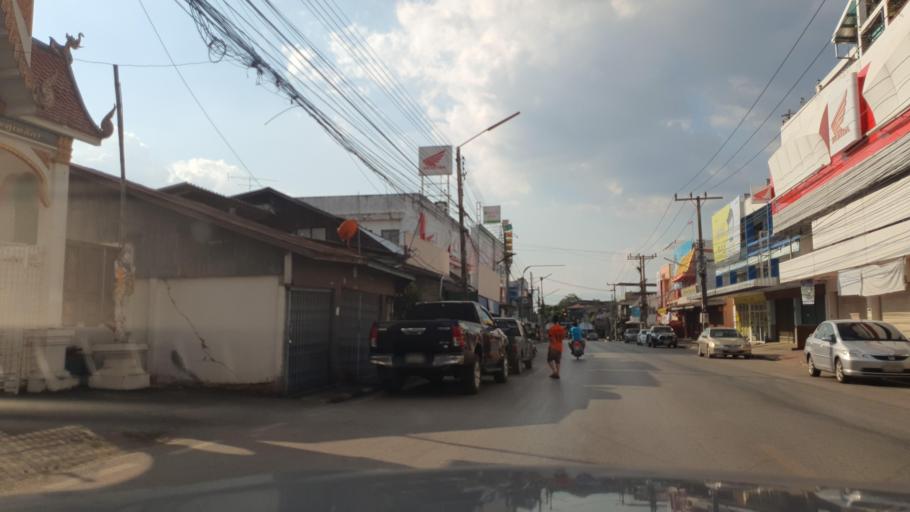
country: TH
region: Phayao
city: Phayao
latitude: 19.1695
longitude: 99.8987
